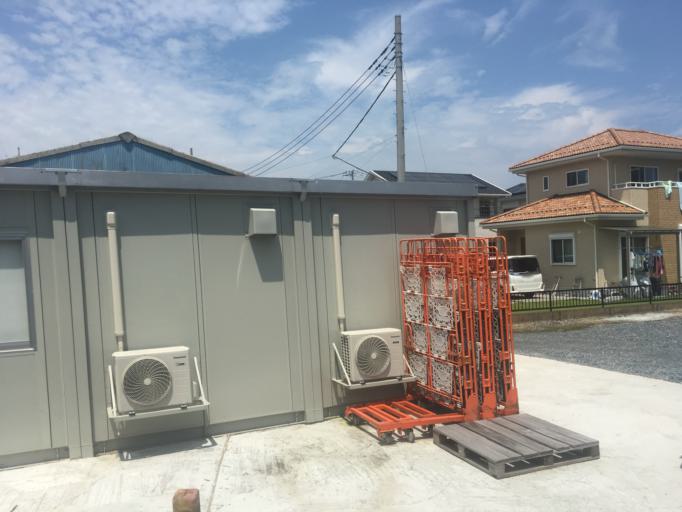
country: JP
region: Saitama
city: Kodamacho-kodamaminami
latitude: 36.1865
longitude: 139.1468
